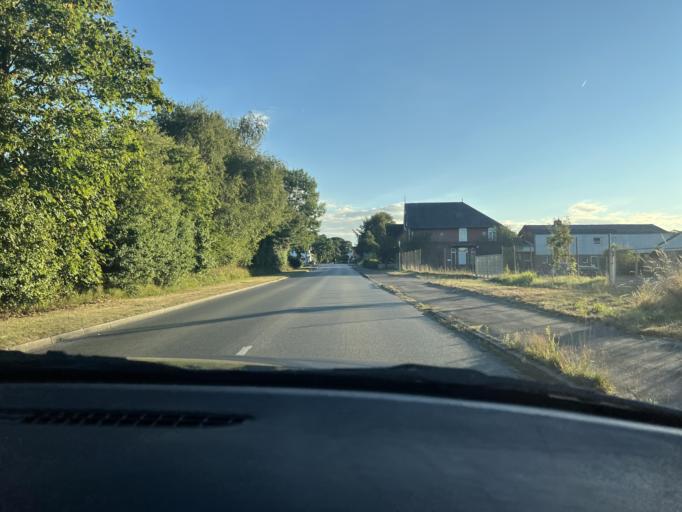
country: DE
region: Schleswig-Holstein
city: Norderheistedt
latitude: 54.2361
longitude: 9.1508
